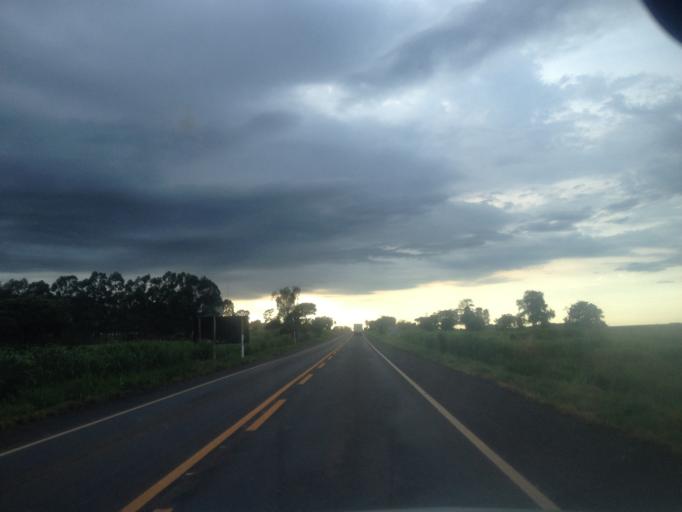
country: BR
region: Goias
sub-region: Jatai
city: Jatai
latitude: -17.8021
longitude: -52.0456
